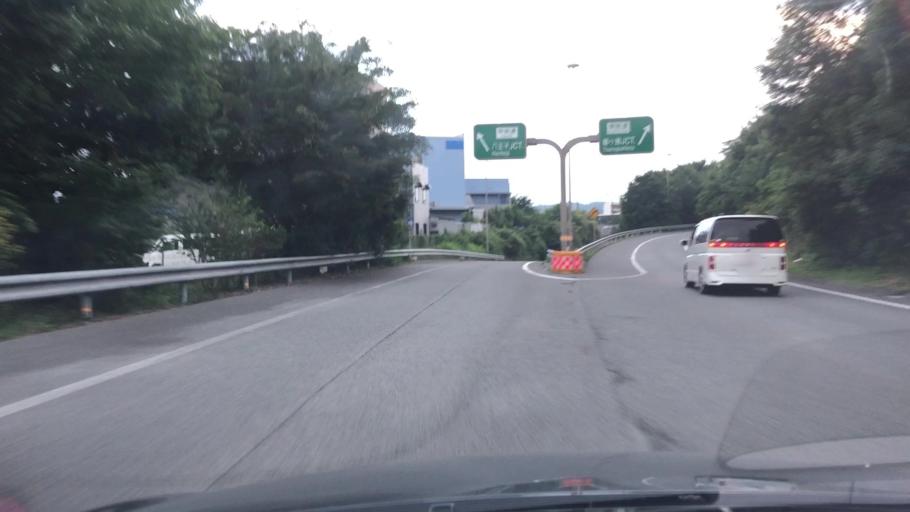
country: JP
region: Tokyo
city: Fussa
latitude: 35.7362
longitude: 139.2837
